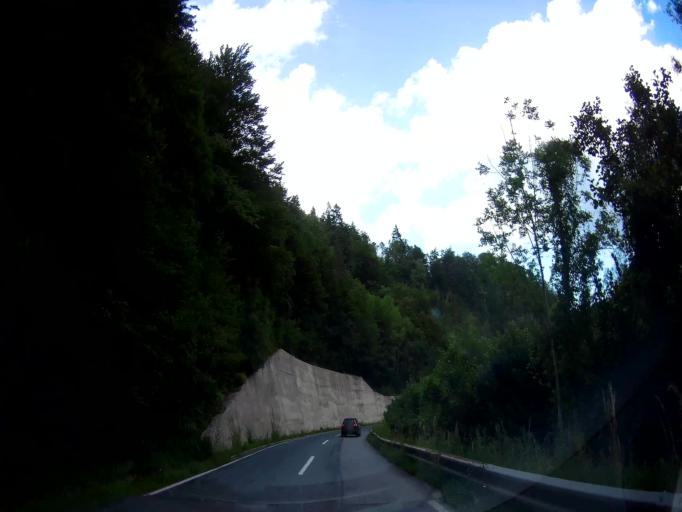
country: AT
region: Carinthia
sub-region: Politischer Bezirk Volkermarkt
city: Sittersdorf
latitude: 46.5285
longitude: 14.5835
